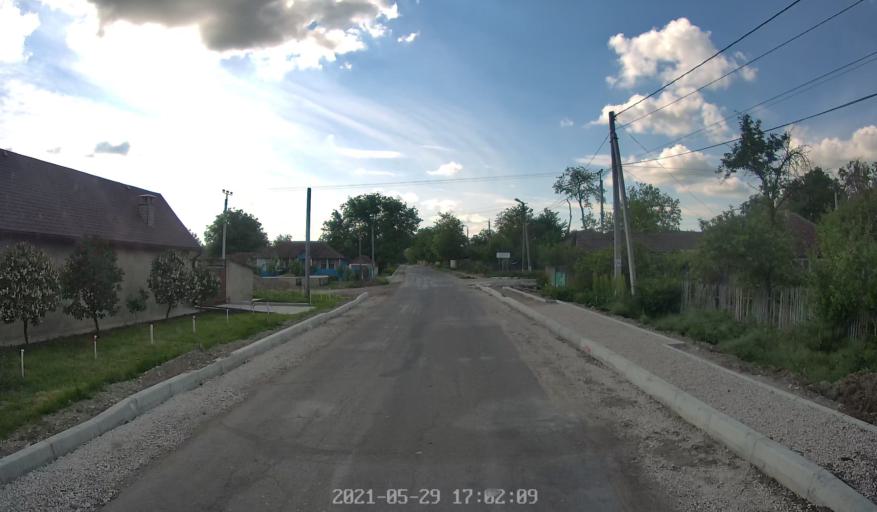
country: MD
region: Laloveni
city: Ialoveni
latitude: 46.8343
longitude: 28.8534
